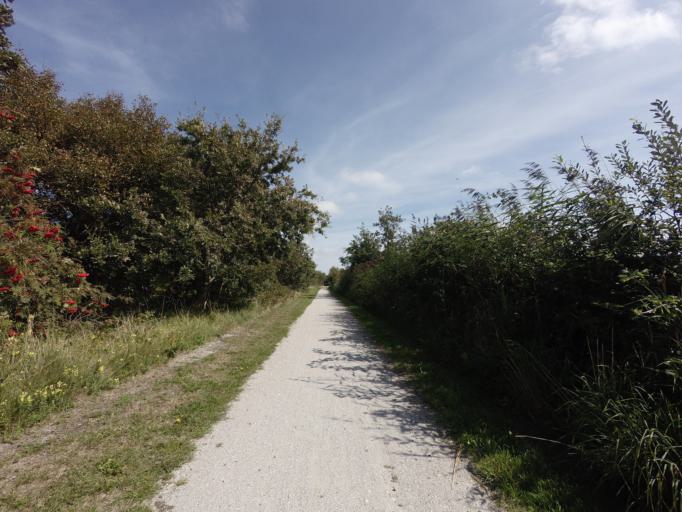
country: NL
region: Friesland
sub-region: Gemeente Ameland
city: Hollum
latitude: 53.4513
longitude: 5.6463
